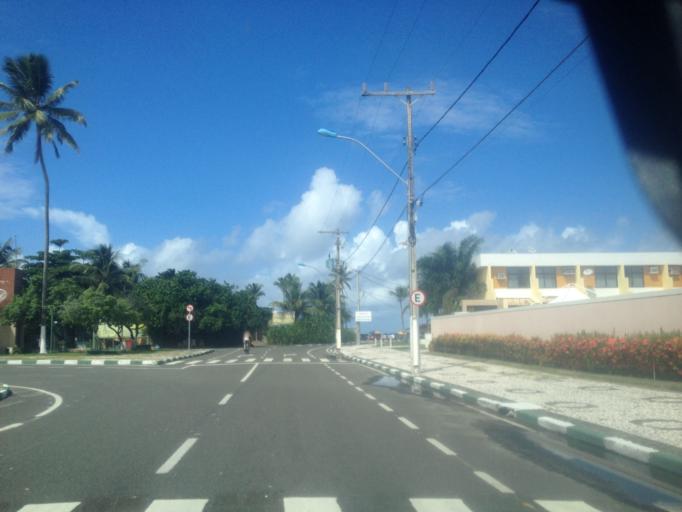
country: BR
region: Bahia
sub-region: Camacari
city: Camacari
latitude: -12.6513
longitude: -38.0697
